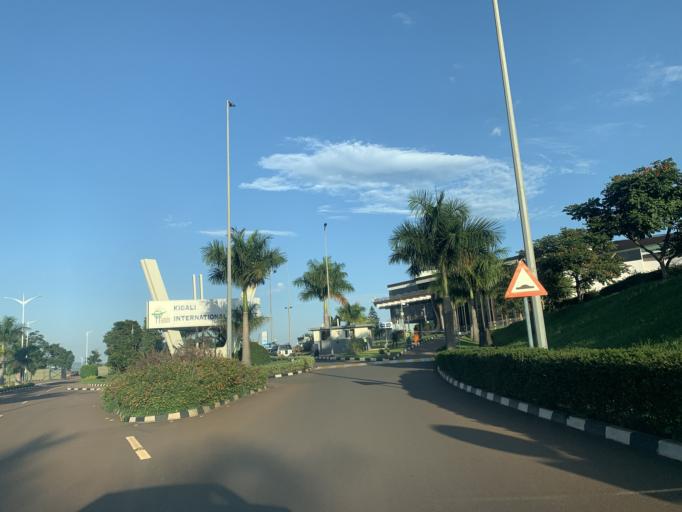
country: RW
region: Kigali
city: Kigali
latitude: -1.9630
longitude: 30.1336
